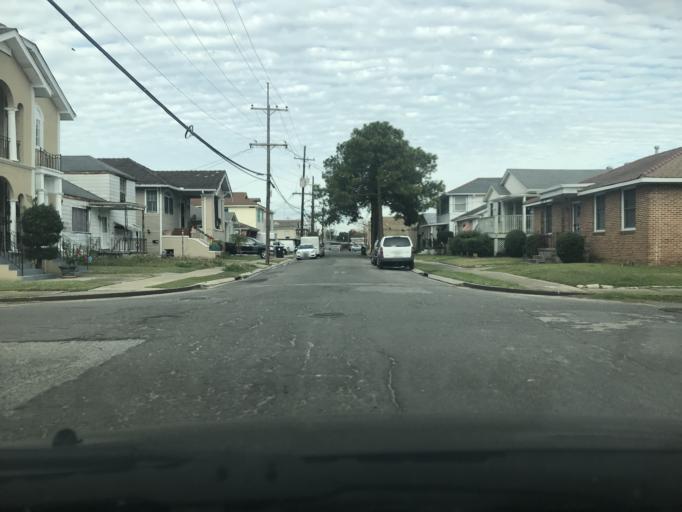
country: US
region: Louisiana
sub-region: Orleans Parish
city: New Orleans
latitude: 29.9529
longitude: -90.1039
